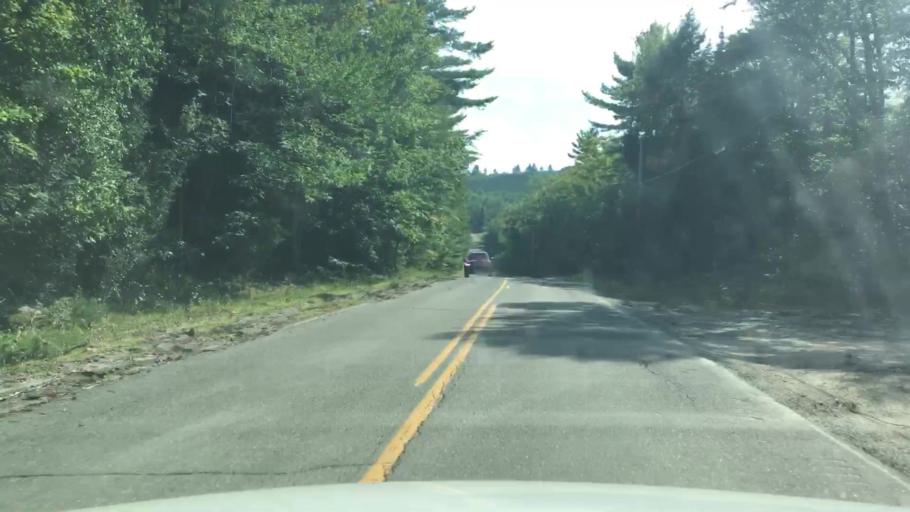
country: US
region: Maine
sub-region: Penobscot County
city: Enfield
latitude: 45.2977
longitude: -68.5531
